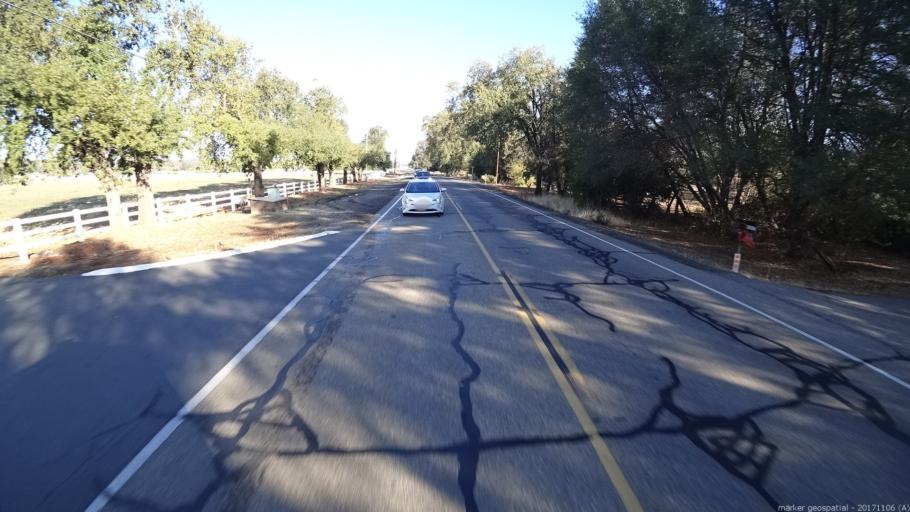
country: US
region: California
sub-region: Shasta County
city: Palo Cedro
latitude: 40.5261
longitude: -122.2385
